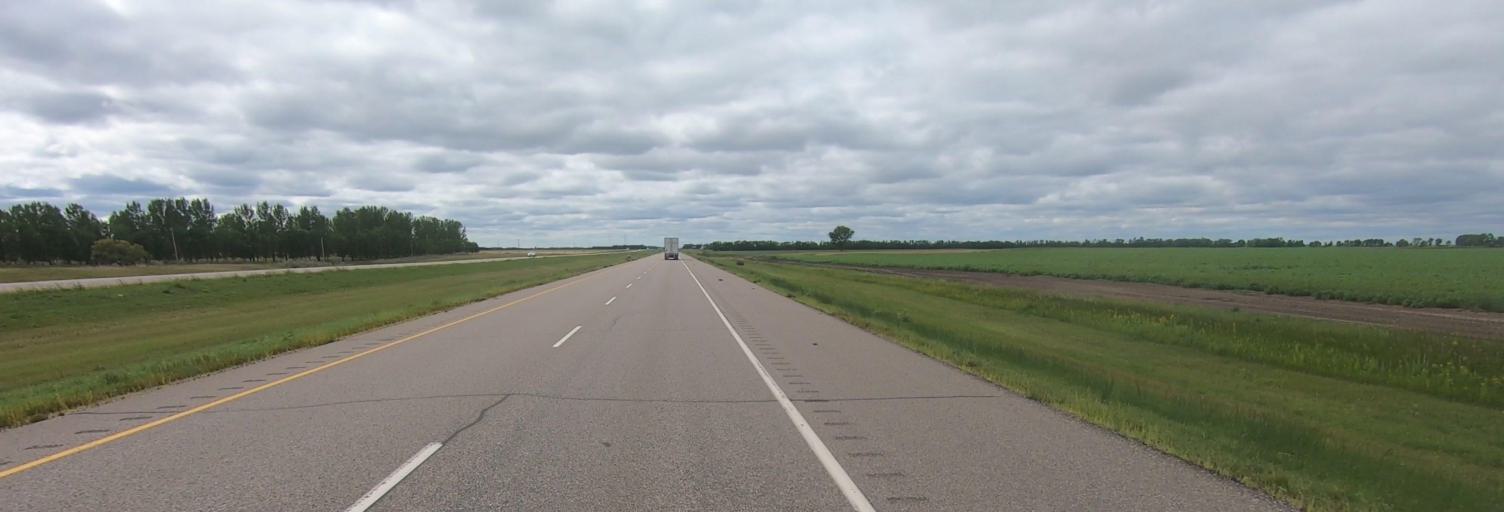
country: CA
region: Manitoba
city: Carberry
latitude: 49.9016
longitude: -99.2859
